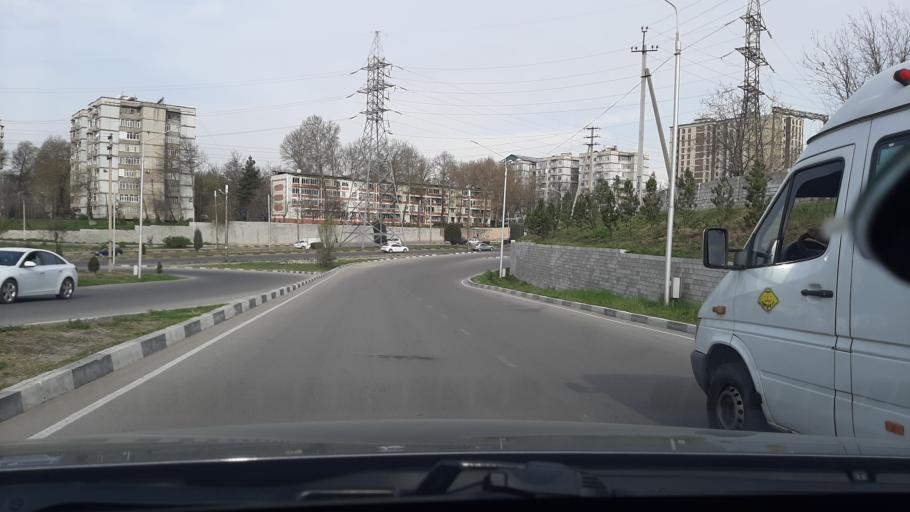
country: TJ
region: Dushanbe
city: Dushanbe
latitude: 38.5686
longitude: 68.7424
